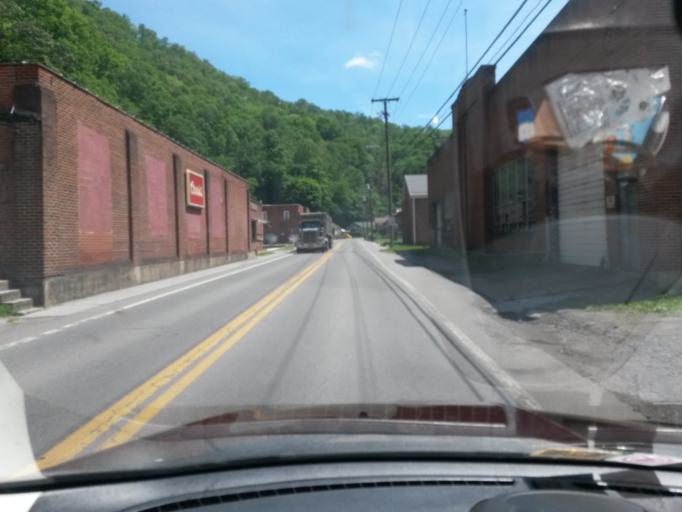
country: US
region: West Virginia
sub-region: McDowell County
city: Welch
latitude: 37.4393
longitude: -81.5867
